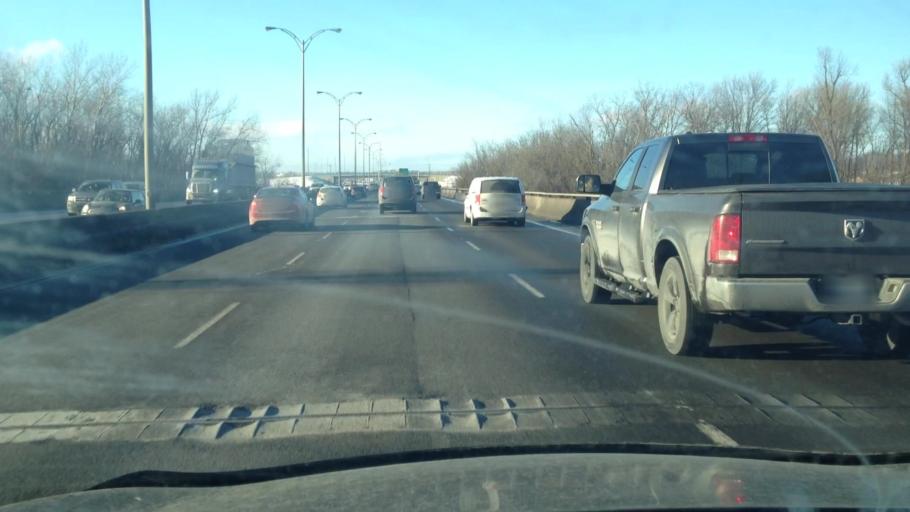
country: CA
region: Quebec
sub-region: Laurentides
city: Boisbriand
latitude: 45.6120
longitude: -73.8151
